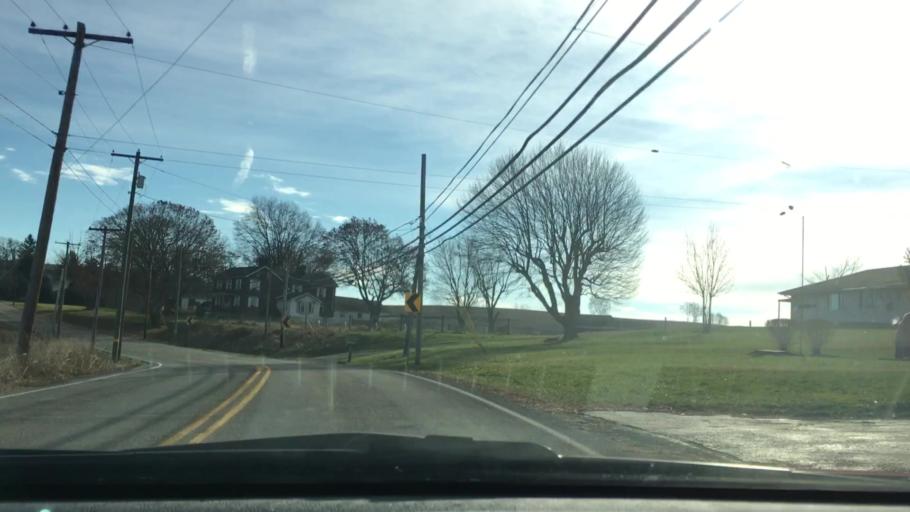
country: US
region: Pennsylvania
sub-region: Westmoreland County
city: West Newton
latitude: 40.1968
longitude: -79.7399
